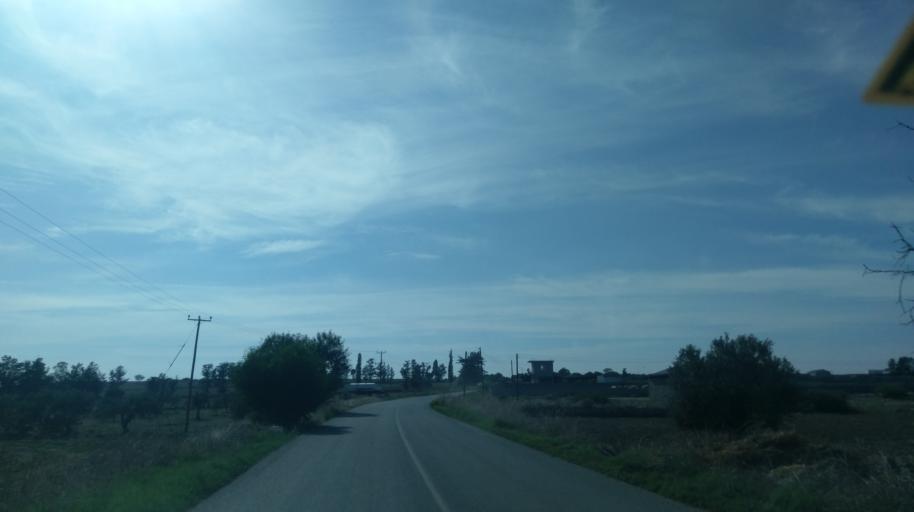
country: CY
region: Ammochostos
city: Lefkonoiko
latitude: 35.2433
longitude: 33.6840
